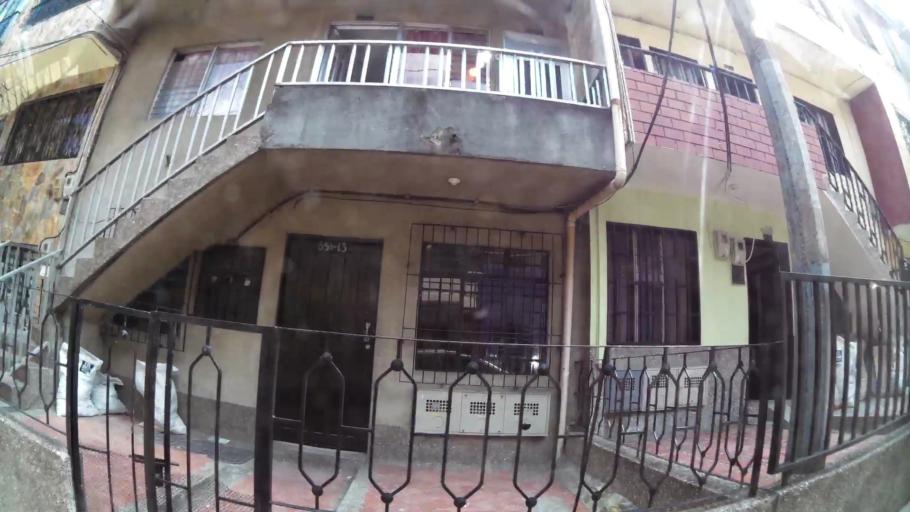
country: CO
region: Antioquia
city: Medellin
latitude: 6.2858
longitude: -75.5718
